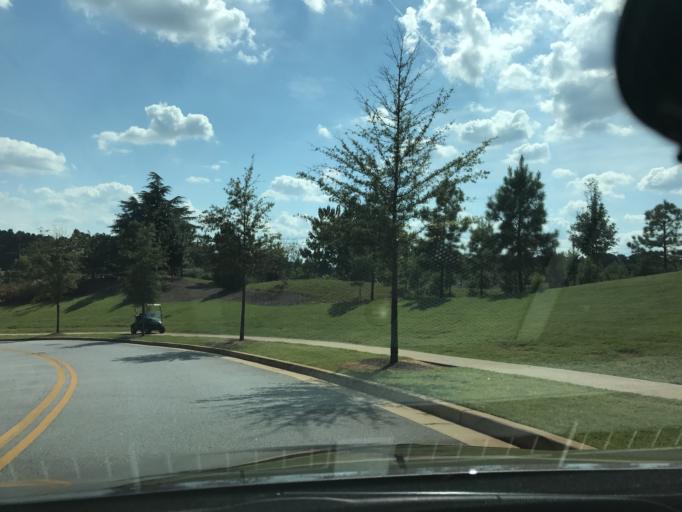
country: US
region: Georgia
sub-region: DeKalb County
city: Decatur
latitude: 33.7458
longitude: -84.3134
